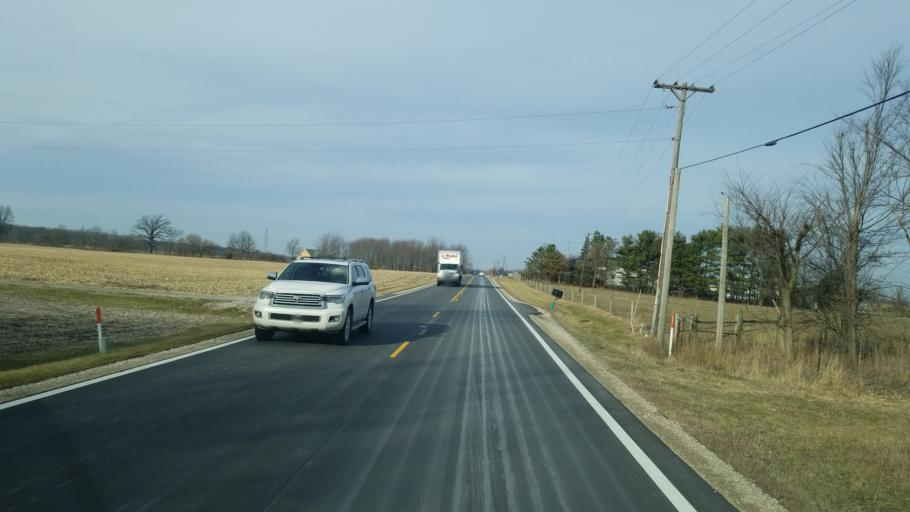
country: US
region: Ohio
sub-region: Union County
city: Marysville
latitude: 40.3526
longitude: -83.3981
